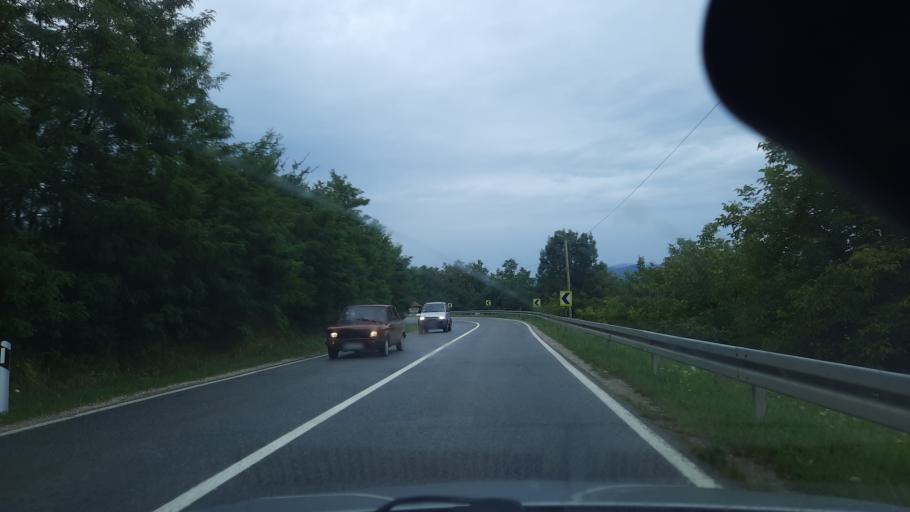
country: RS
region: Central Serbia
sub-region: Sumadijski Okrug
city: Knic
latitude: 43.9003
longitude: 20.7645
